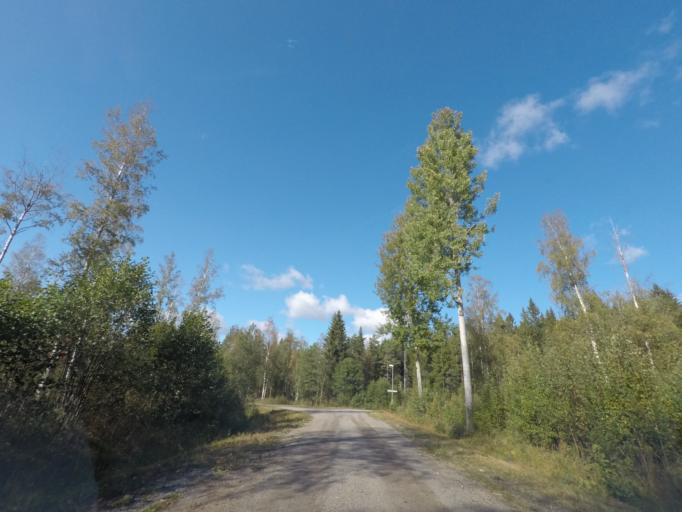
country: SE
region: Vaestmanland
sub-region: Skinnskattebergs Kommun
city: Skinnskatteberg
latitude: 59.8306
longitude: 15.5207
